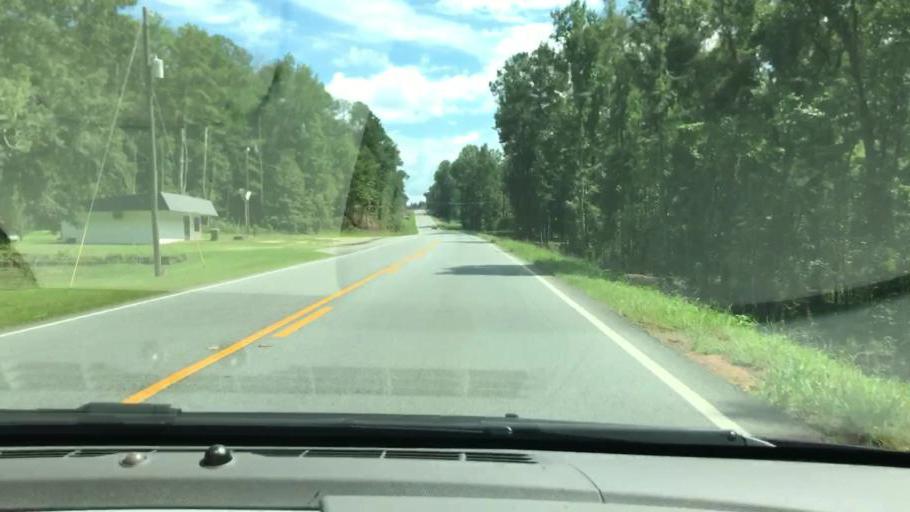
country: US
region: Georgia
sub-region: Quitman County
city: Georgetown
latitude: 31.8720
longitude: -85.0789
